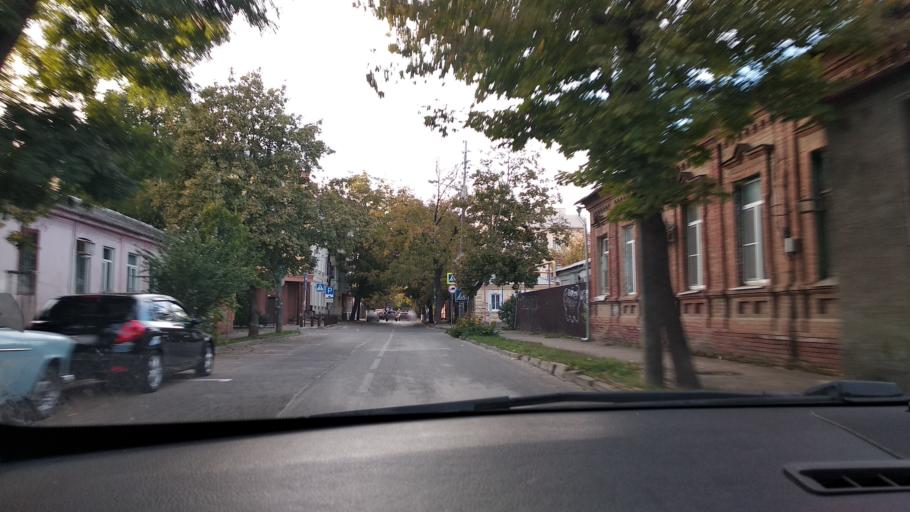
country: RU
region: Krasnodarskiy
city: Krasnodar
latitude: 45.0269
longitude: 38.9807
